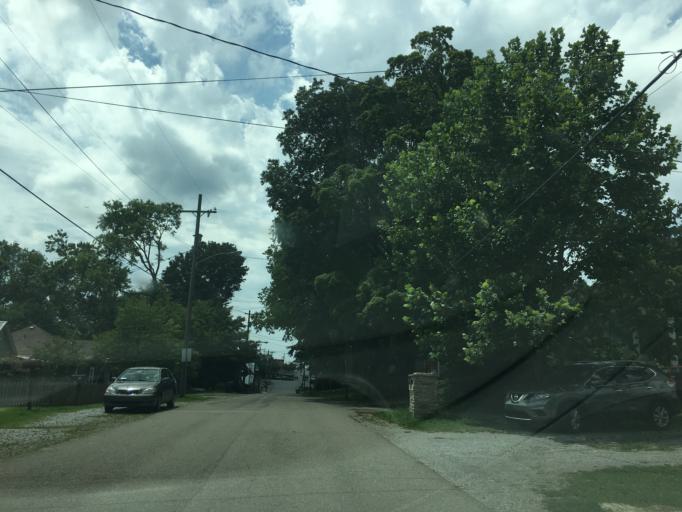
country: US
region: Tennessee
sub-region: Davidson County
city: Oak Hill
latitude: 36.1176
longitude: -86.7458
